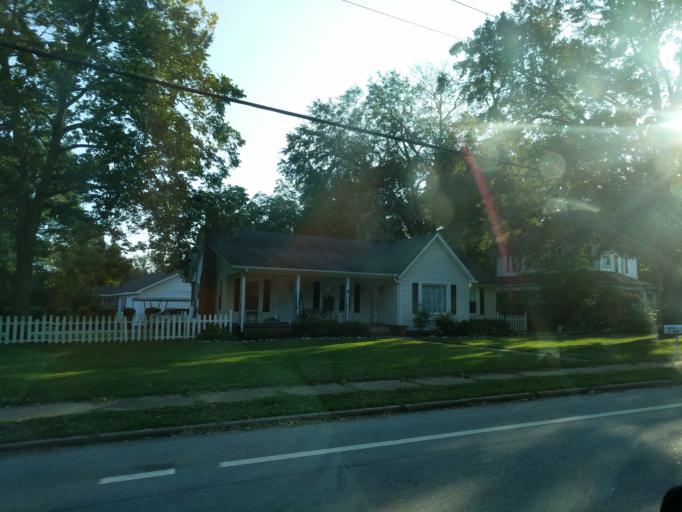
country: US
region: South Carolina
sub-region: Anderson County
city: Williamston
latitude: 34.6456
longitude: -82.4738
